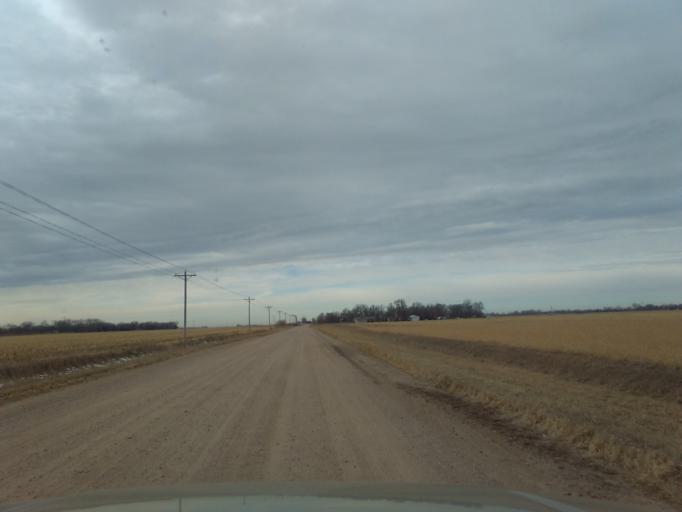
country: US
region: Nebraska
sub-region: Buffalo County
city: Gibbon
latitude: 40.6477
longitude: -98.8497
